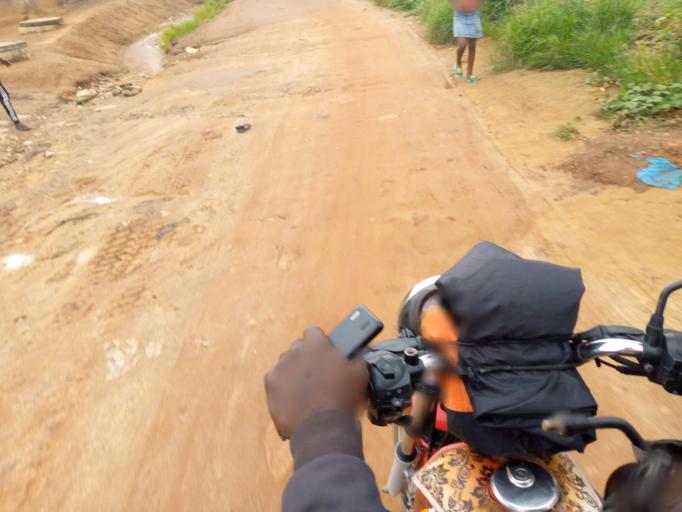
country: SL
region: Eastern Province
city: Kenema
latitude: 7.8700
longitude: -11.1890
